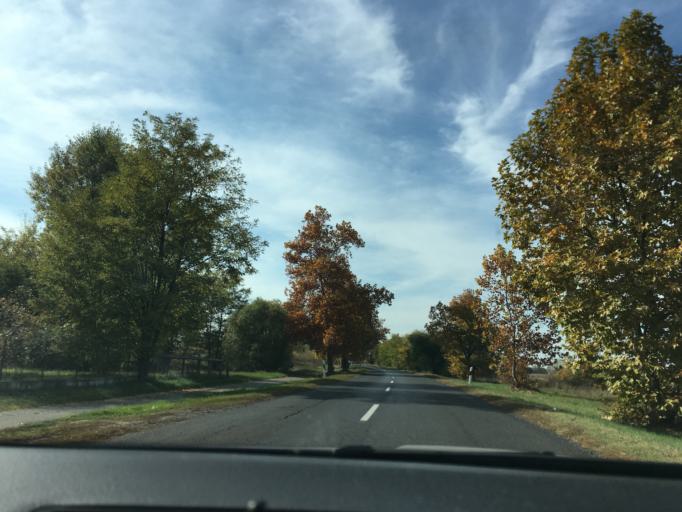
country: HU
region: Hajdu-Bihar
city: Vamospercs
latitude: 47.5270
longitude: 21.9267
